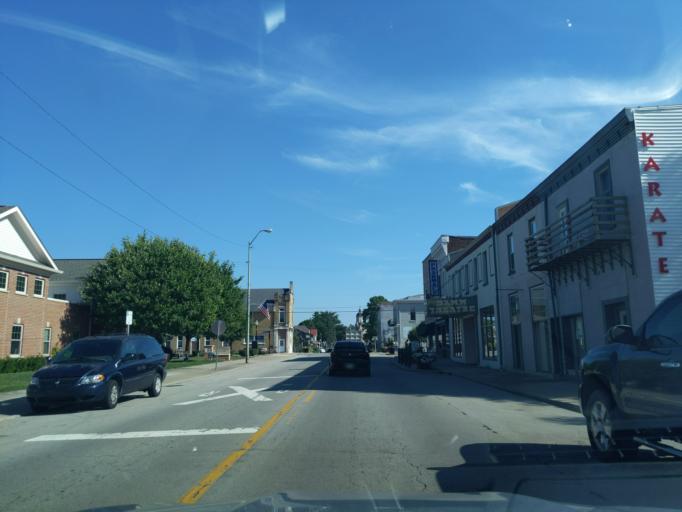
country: US
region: Indiana
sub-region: Ripley County
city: Osgood
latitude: 39.1300
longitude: -85.2917
